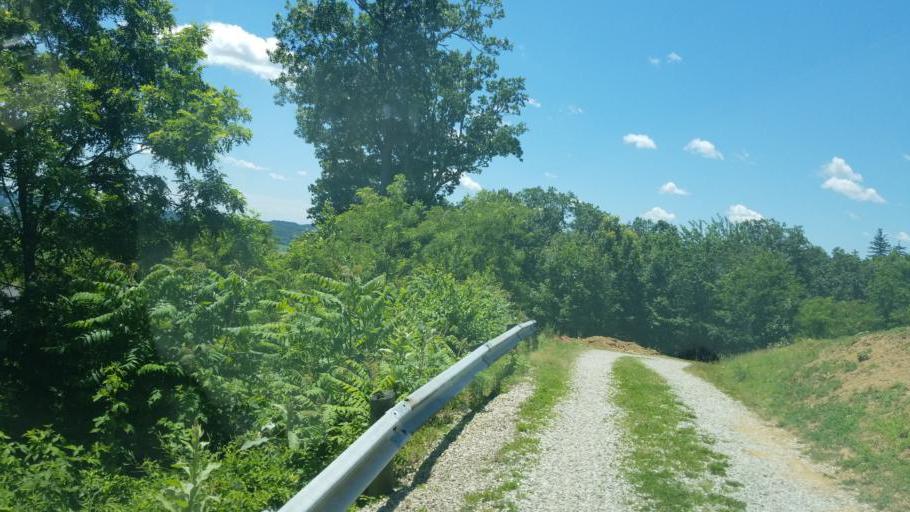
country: US
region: Ohio
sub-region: Gallia County
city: Gallipolis
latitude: 38.7998
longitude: -82.2198
